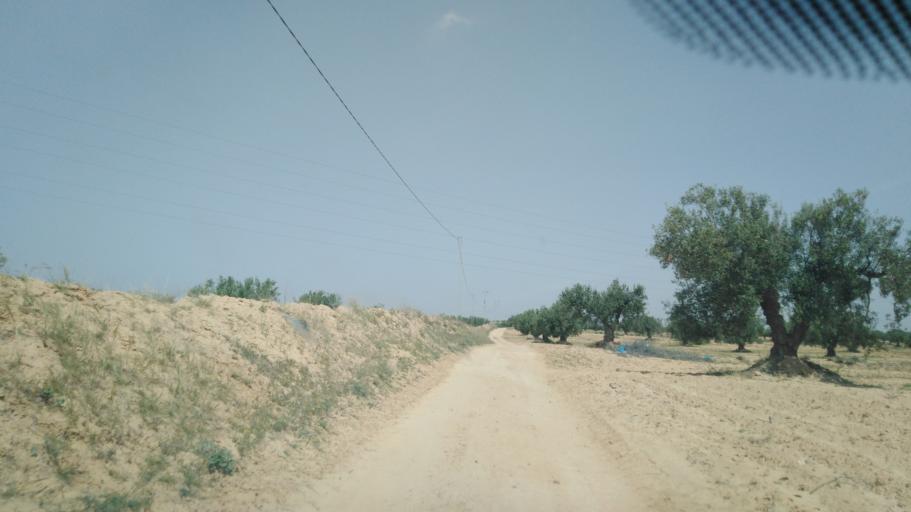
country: TN
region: Safaqis
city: Sfax
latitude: 34.7407
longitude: 10.5716
